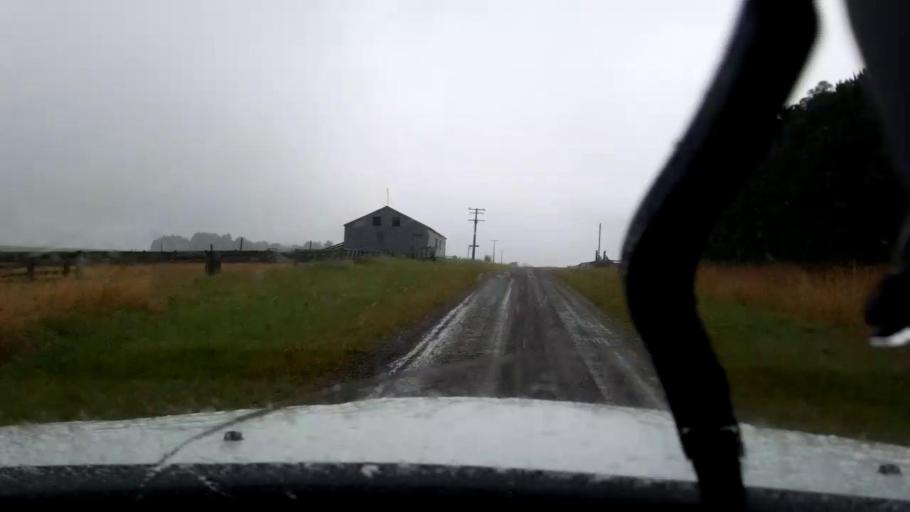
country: NZ
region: Canterbury
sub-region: Timaru District
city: Pleasant Point
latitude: -44.1700
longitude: 171.1457
